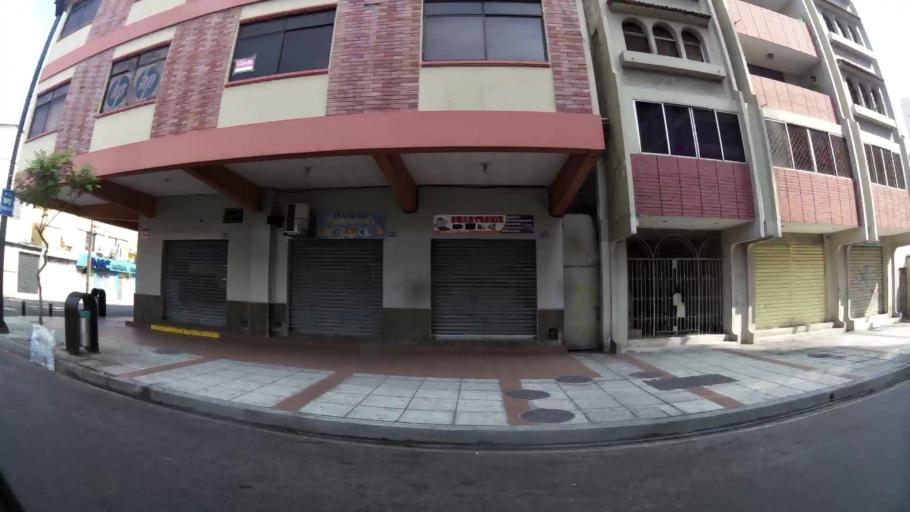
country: EC
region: Guayas
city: Guayaquil
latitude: -2.1879
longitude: -79.8965
